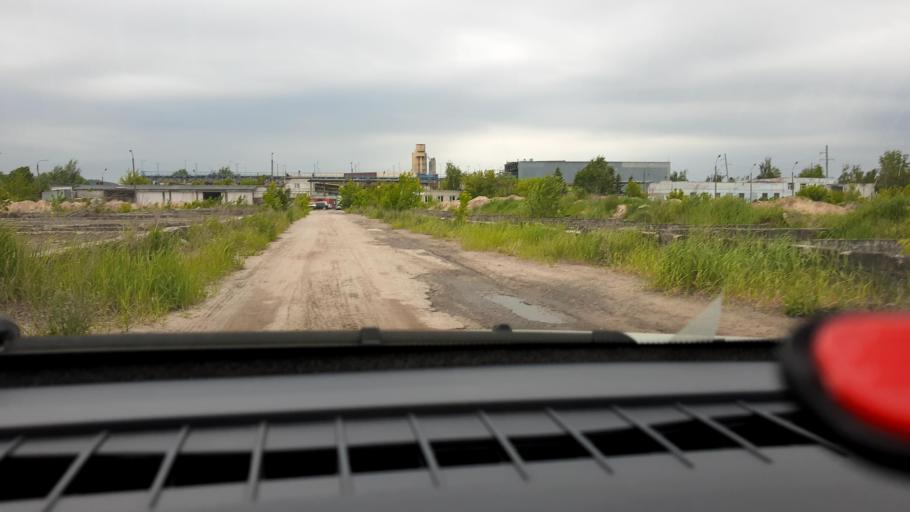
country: RU
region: Nizjnij Novgorod
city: Nizhniy Novgorod
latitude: 56.2428
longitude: 43.9283
